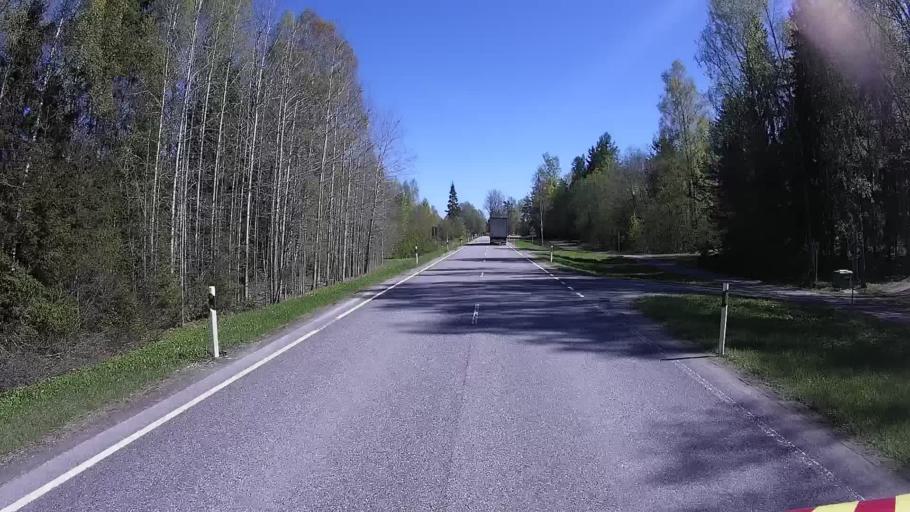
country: EE
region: Harju
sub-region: Kuusalu vald
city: Kuusalu
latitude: 59.2689
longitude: 25.6530
